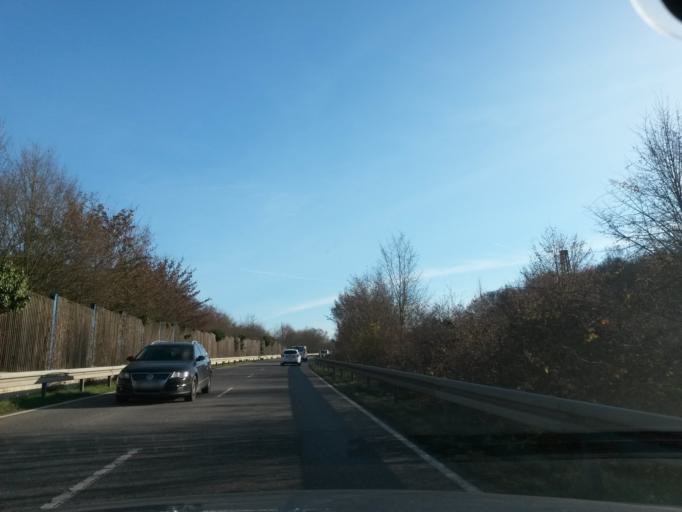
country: DE
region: Baden-Wuerttemberg
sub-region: Karlsruhe Region
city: Ispringen
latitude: 48.9134
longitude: 8.6747
